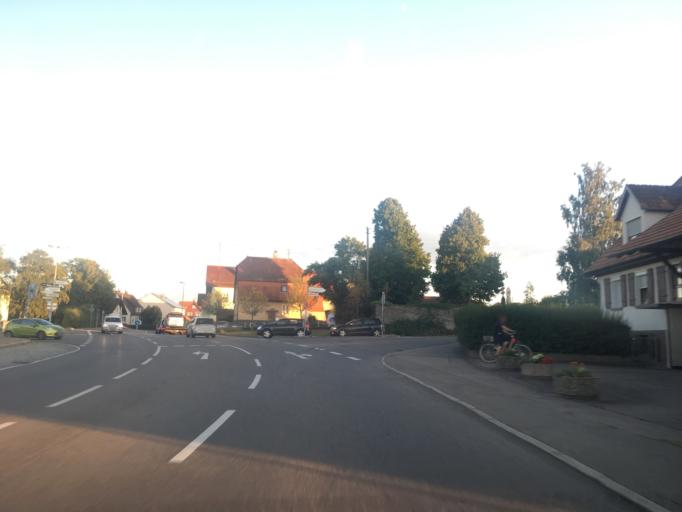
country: DE
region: Baden-Wuerttemberg
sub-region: Tuebingen Region
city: Sankt Johann
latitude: 48.3888
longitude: 9.2930
